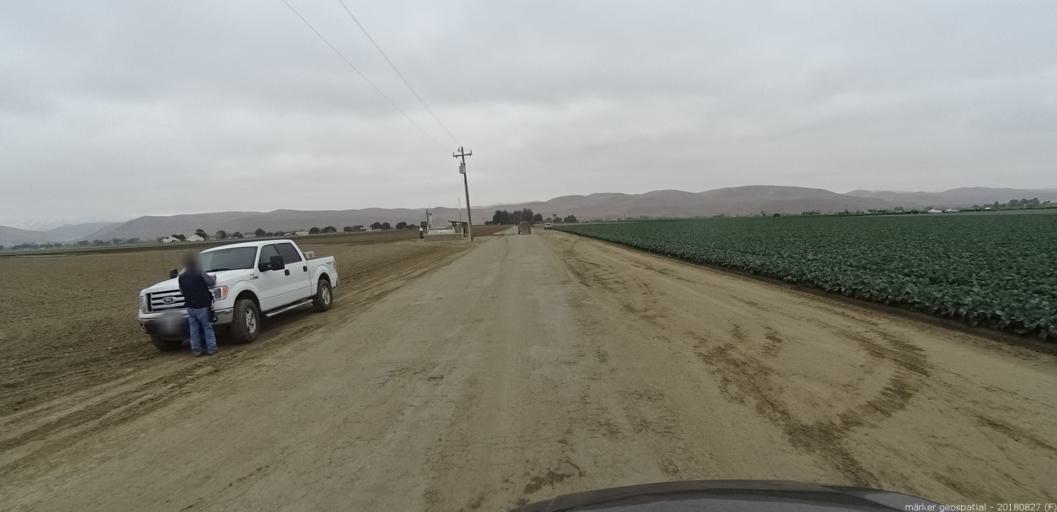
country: US
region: California
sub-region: Monterey County
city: Greenfield
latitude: 36.3200
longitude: -121.2089
